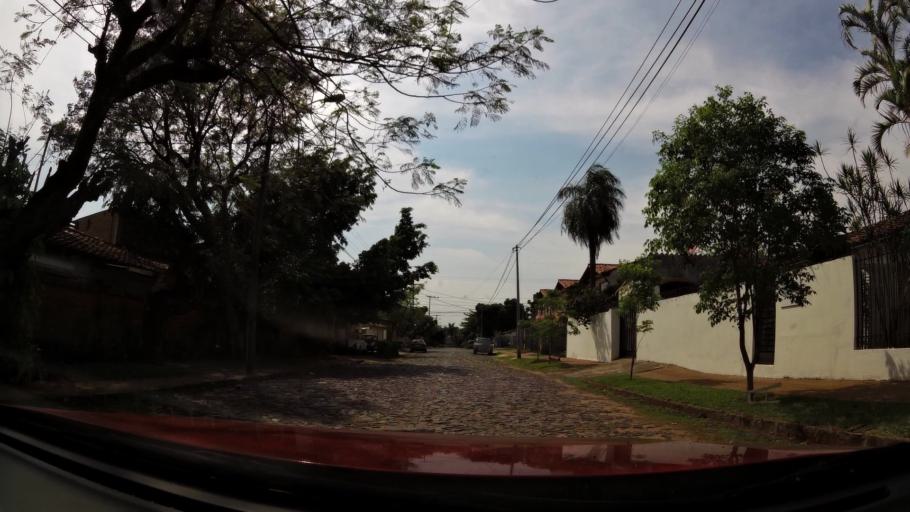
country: PY
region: Asuncion
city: Asuncion
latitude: -25.2663
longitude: -57.5666
